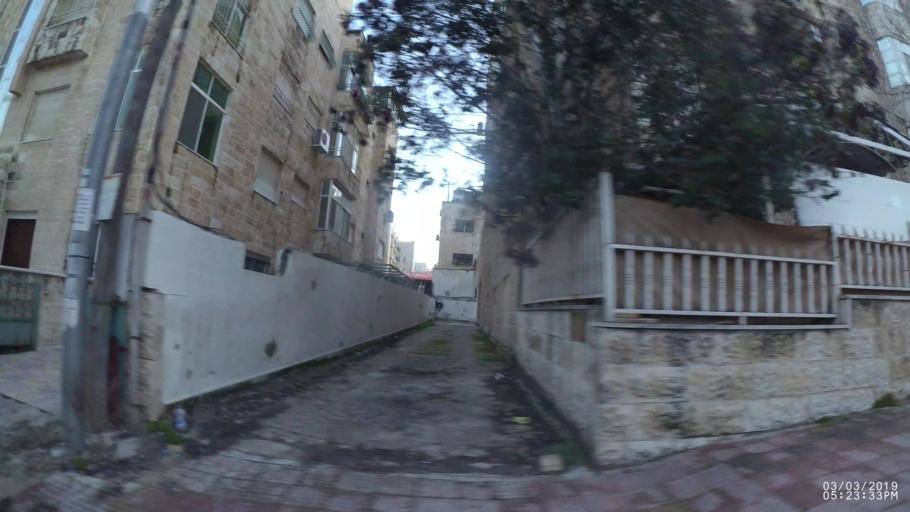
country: JO
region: Amman
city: Al Jubayhah
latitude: 31.9866
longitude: 35.8837
